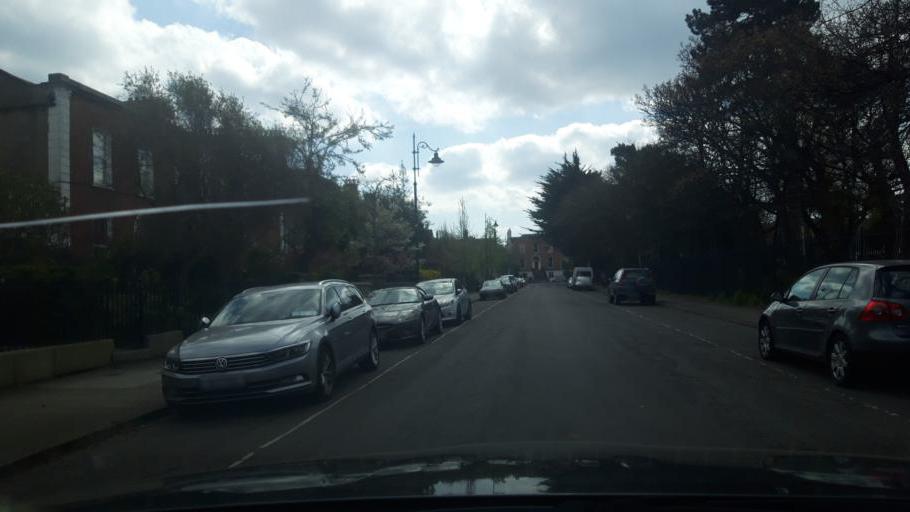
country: IE
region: Leinster
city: Rathgar
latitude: 53.3188
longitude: -6.2748
